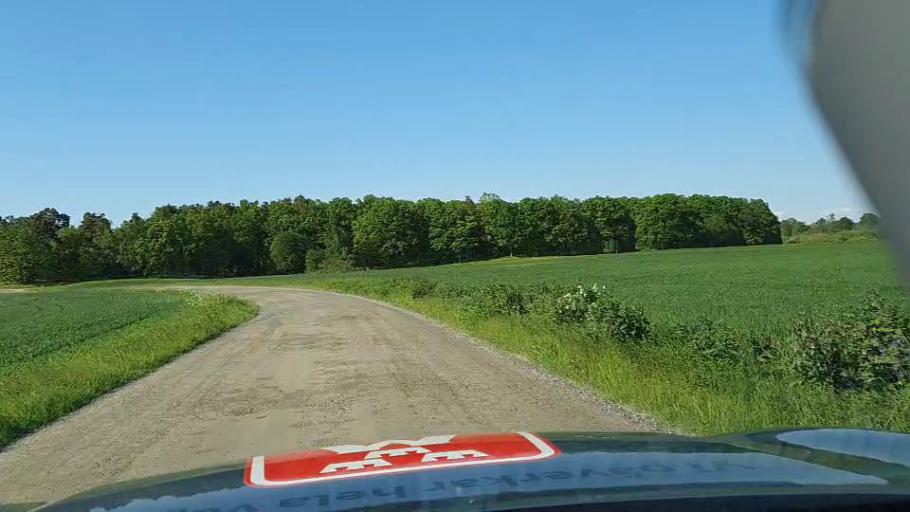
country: SE
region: Skane
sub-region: Hassleholms Kommun
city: Tormestorp
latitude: 56.1138
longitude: 13.7187
